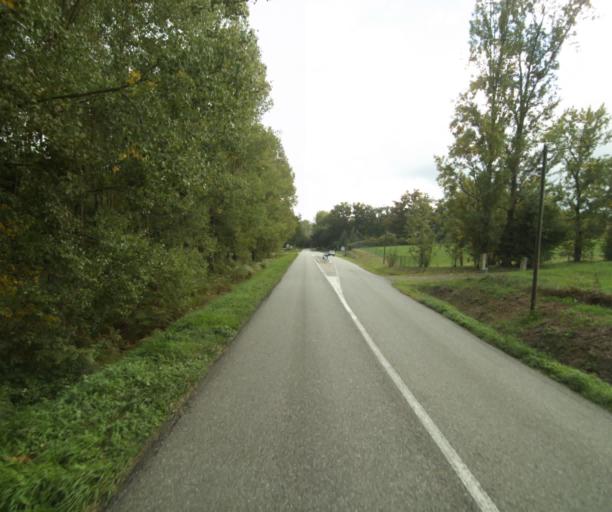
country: FR
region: Midi-Pyrenees
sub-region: Departement du Gers
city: Eauze
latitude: 43.9002
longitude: 0.0993
